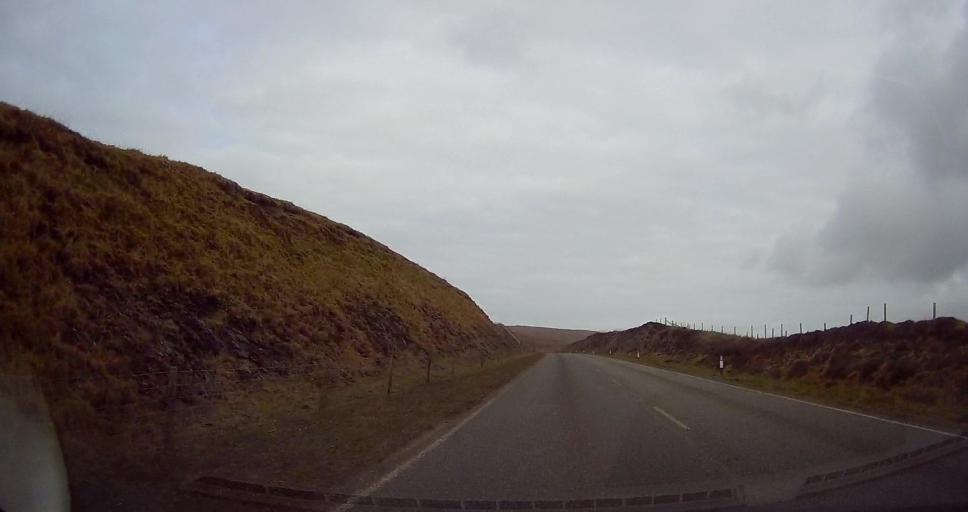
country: GB
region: Scotland
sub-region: Shetland Islands
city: Sandwick
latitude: 60.0658
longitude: -1.2234
